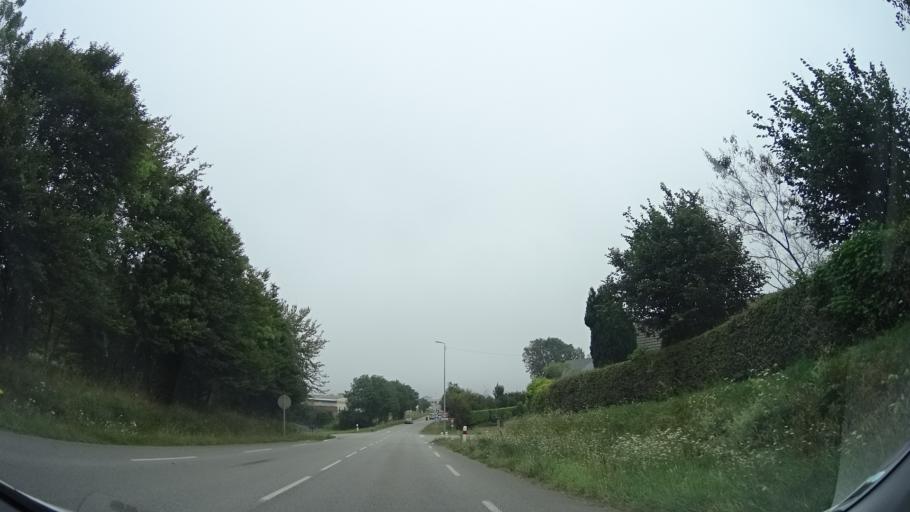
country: FR
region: Lower Normandy
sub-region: Departement de la Manche
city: Les Pieux
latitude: 49.5174
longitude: -1.8031
